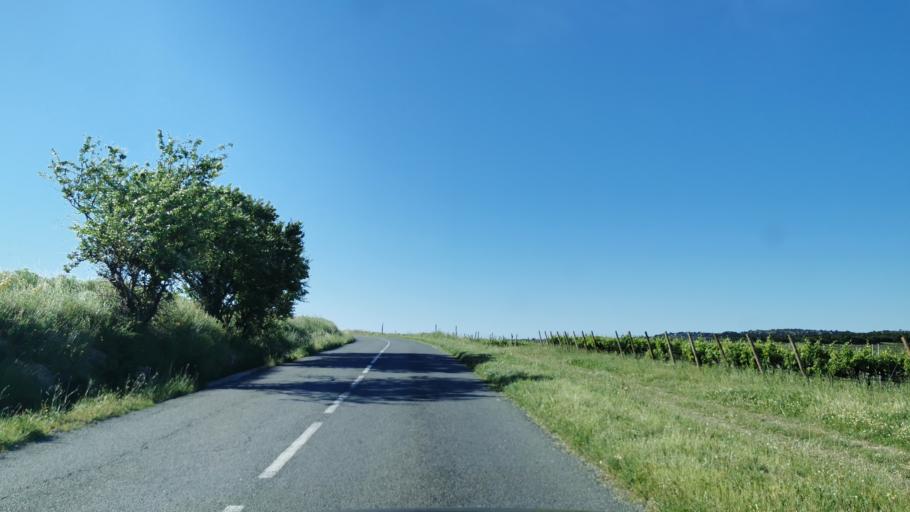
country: FR
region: Languedoc-Roussillon
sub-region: Departement de l'Aude
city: Armissan
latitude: 43.1735
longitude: 3.1117
